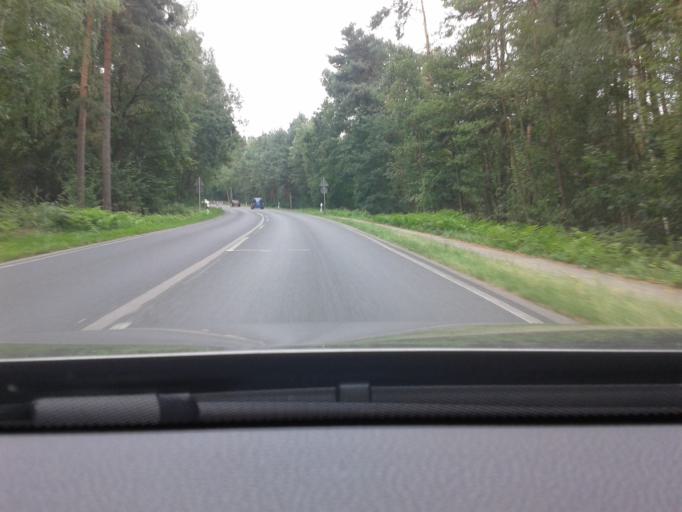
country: DE
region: Lower Saxony
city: Gifhorn
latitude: 52.4940
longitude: 10.5682
